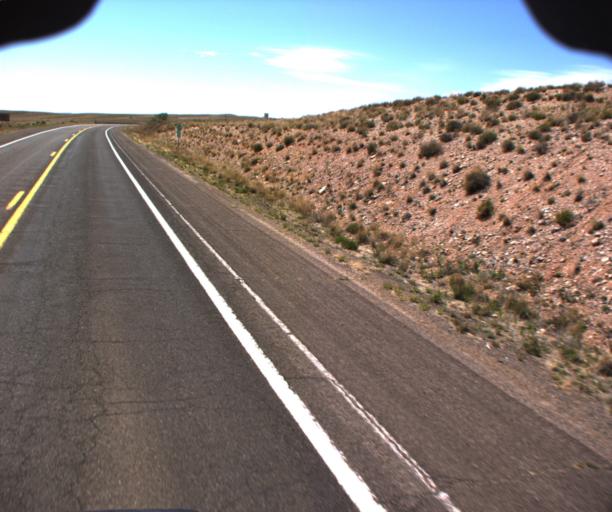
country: US
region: Arizona
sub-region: Mohave County
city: Peach Springs
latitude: 35.5227
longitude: -113.4480
